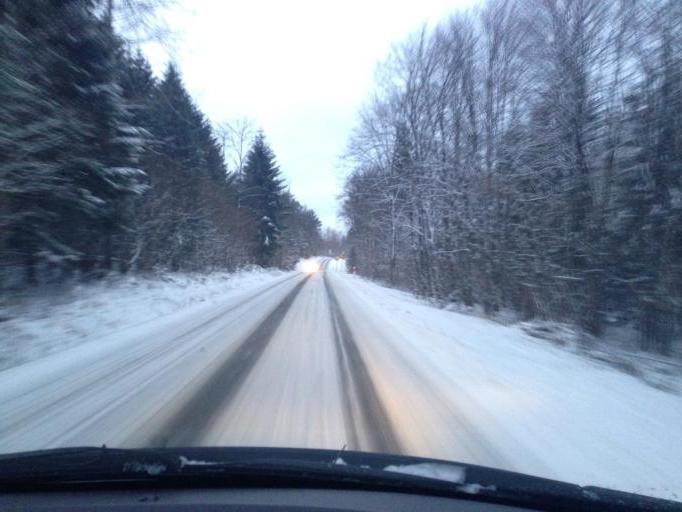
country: PL
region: Subcarpathian Voivodeship
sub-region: Powiat jasielski
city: Krempna
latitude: 49.5364
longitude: 21.5002
